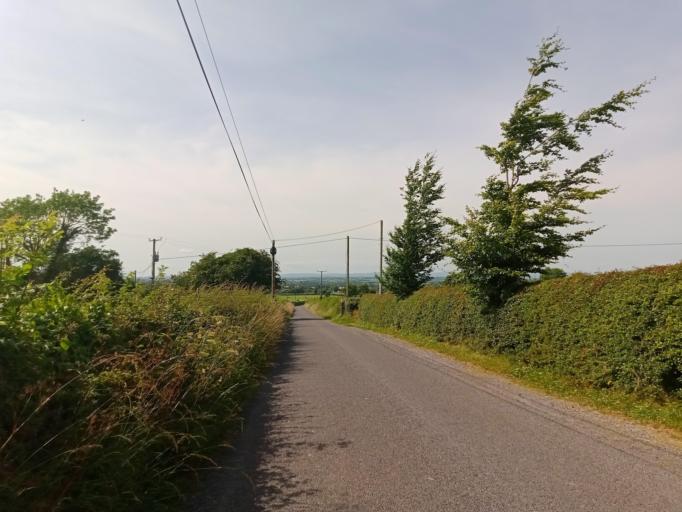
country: IE
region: Leinster
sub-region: Laois
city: Rathdowney
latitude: 52.8071
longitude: -7.4661
